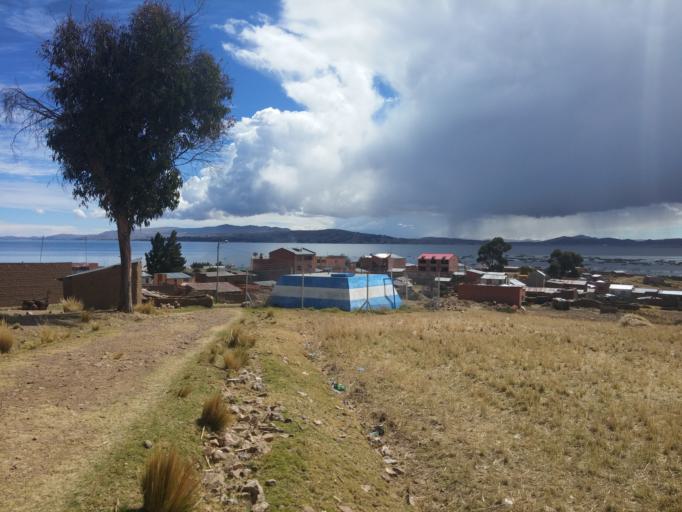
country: BO
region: La Paz
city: Batallas
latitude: -16.2861
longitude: -68.5992
